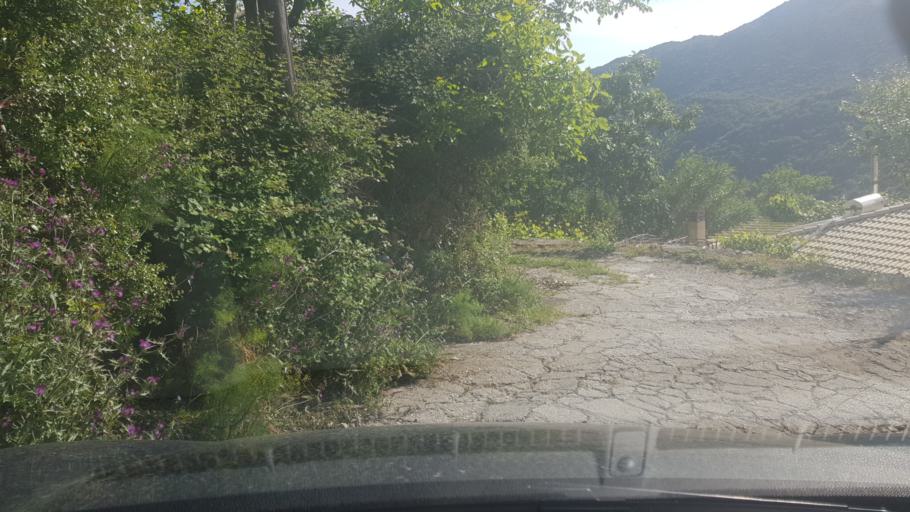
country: GR
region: Ionian Islands
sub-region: Lefkada
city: Nidri
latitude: 38.6883
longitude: 20.6464
